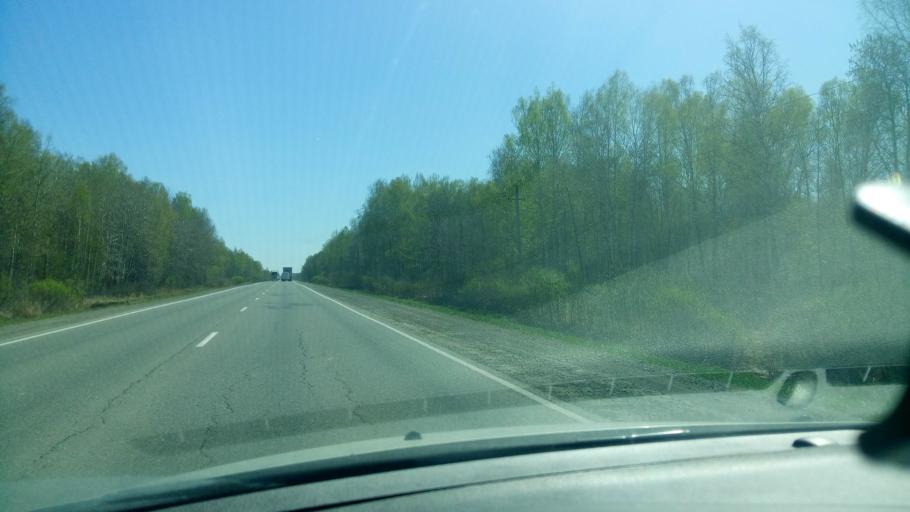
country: RU
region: Sverdlovsk
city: Bogdanovich
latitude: 56.7542
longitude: 62.1746
